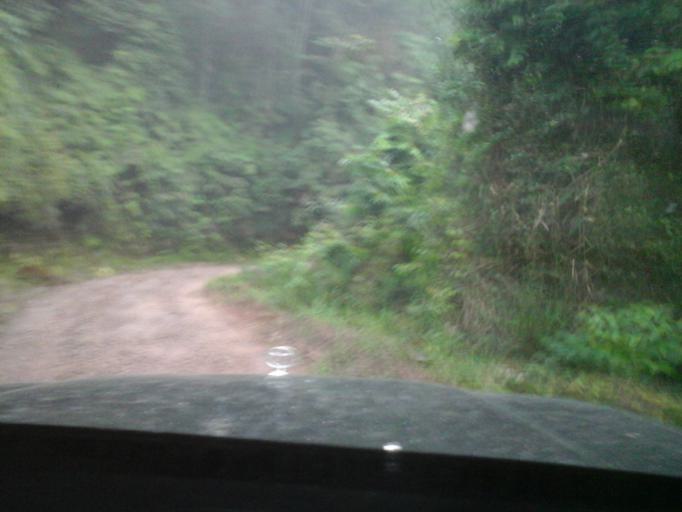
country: CO
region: Cesar
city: Agustin Codazzi
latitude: 9.9387
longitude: -73.1390
